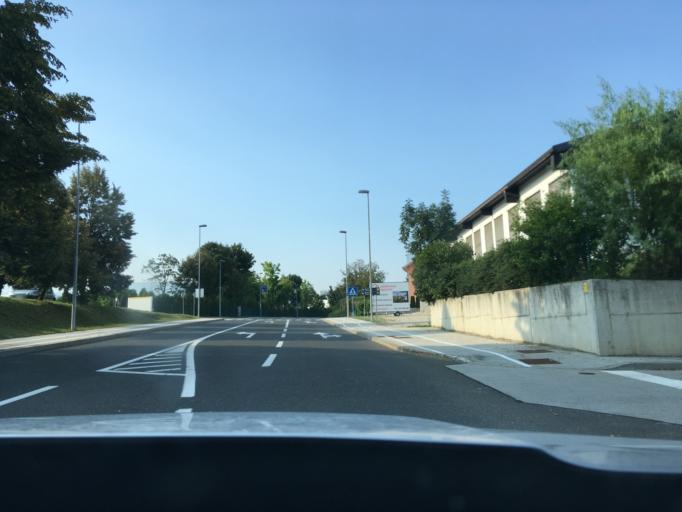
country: SI
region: Novo Mesto
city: Novo Mesto
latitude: 45.7913
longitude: 15.1787
